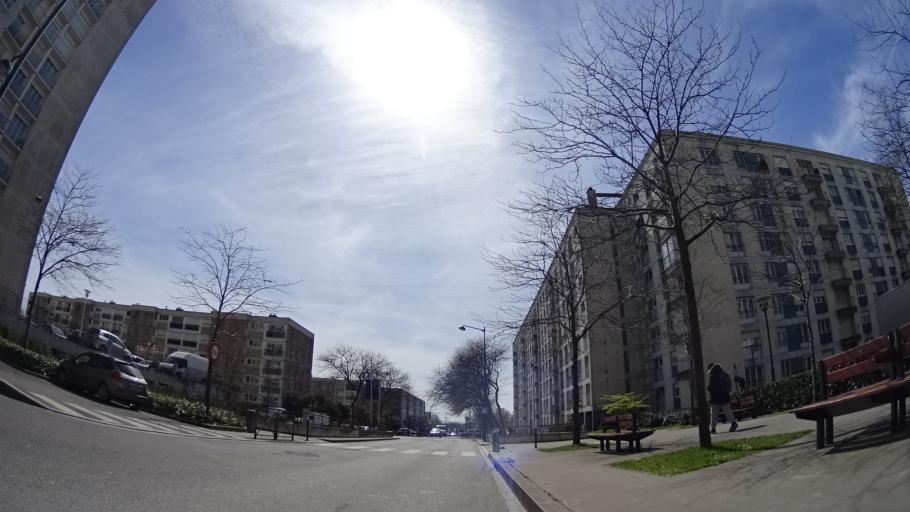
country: FR
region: Brittany
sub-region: Departement d'Ille-et-Vilaine
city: Montgermont
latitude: 48.1209
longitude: -1.7135
